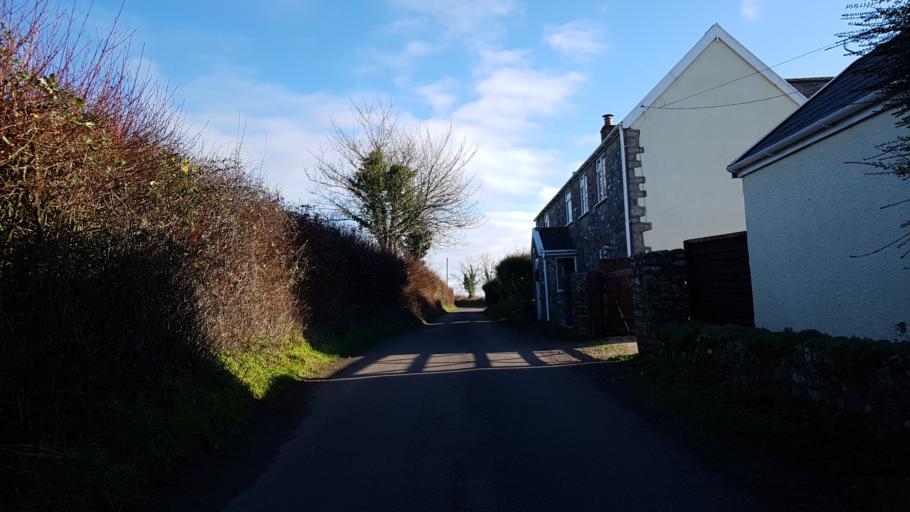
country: GB
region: England
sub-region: Somerset
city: Chard
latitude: 50.8962
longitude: -2.9864
